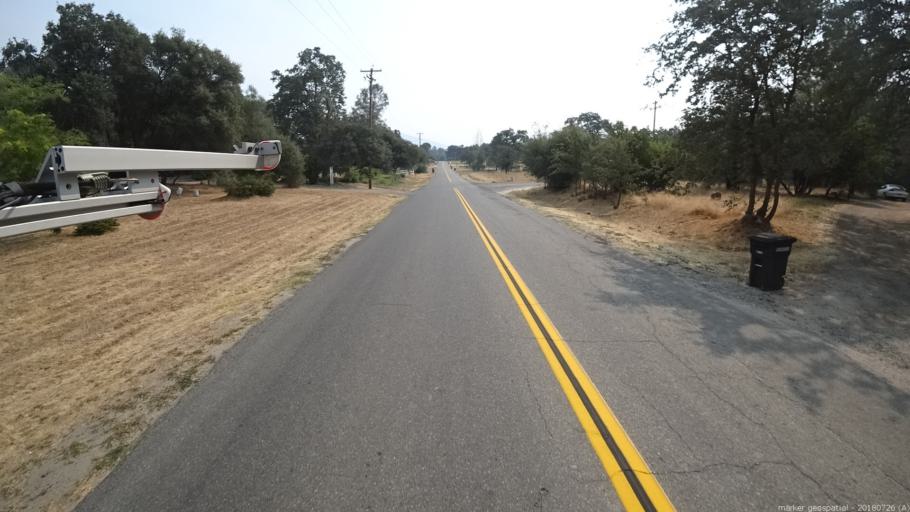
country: US
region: California
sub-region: Madera County
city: Coarsegold
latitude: 37.2125
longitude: -119.6892
